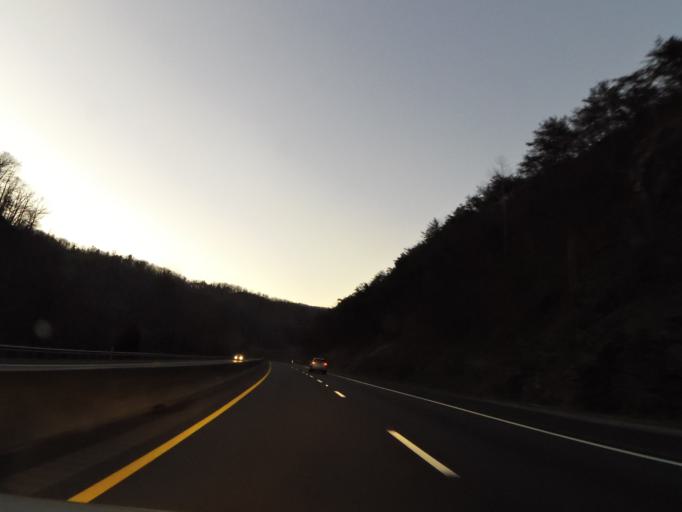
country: US
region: Tennessee
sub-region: Cocke County
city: Newport
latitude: 35.8075
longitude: -83.1391
